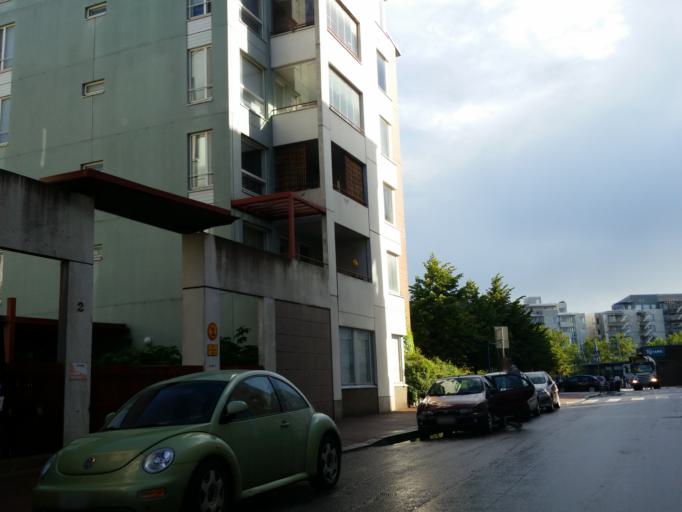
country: FI
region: Uusimaa
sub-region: Helsinki
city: Helsinki
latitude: 60.1628
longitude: 24.9126
